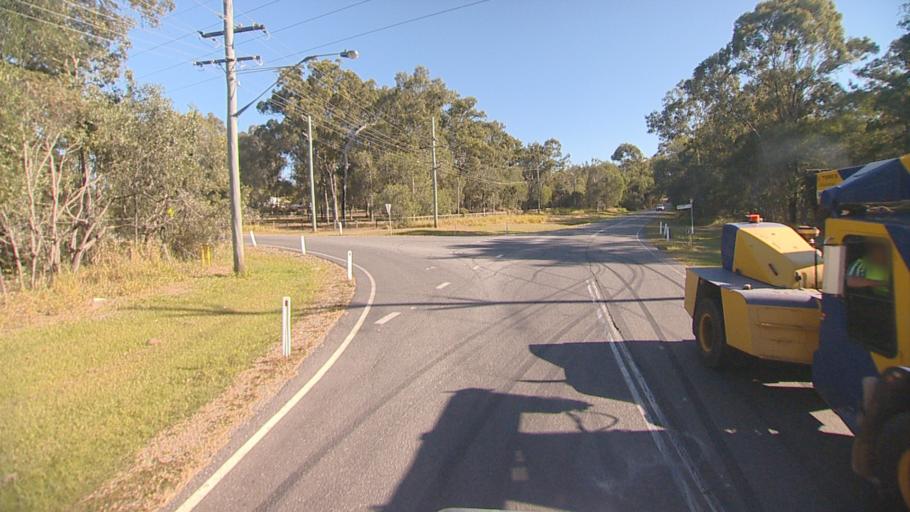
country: AU
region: Queensland
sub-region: Logan
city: North Maclean
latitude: -27.7904
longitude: 153.0421
